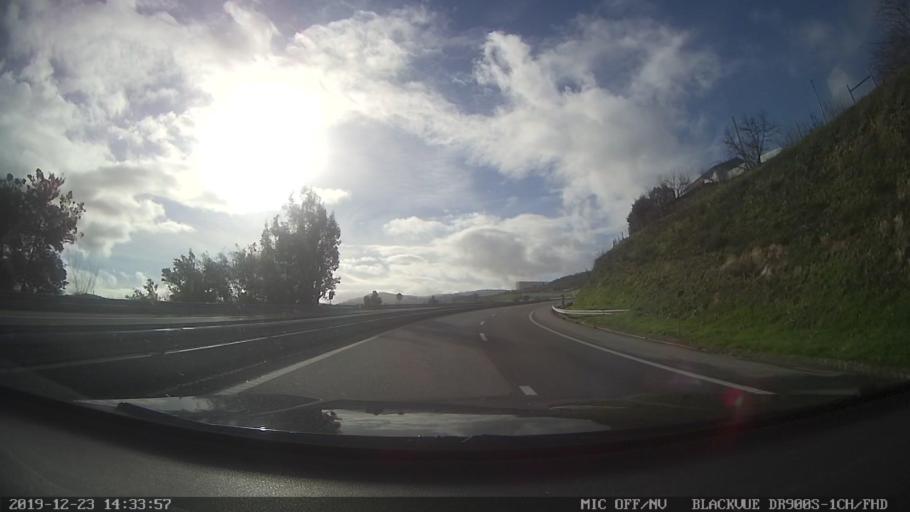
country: PT
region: Viseu
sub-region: Lamego
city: Lamego
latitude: 41.0890
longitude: -7.7840
